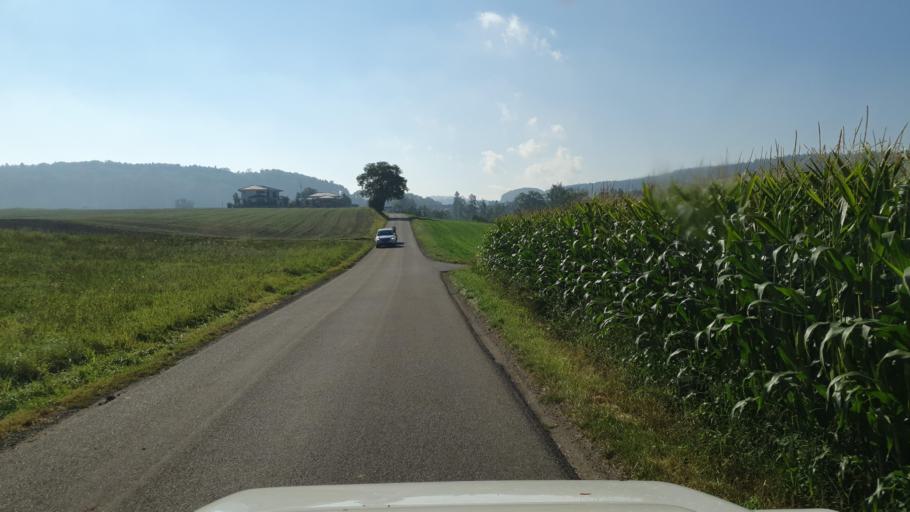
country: CH
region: Aargau
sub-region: Bezirk Bremgarten
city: Villmergen
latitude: 47.3316
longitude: 8.2621
